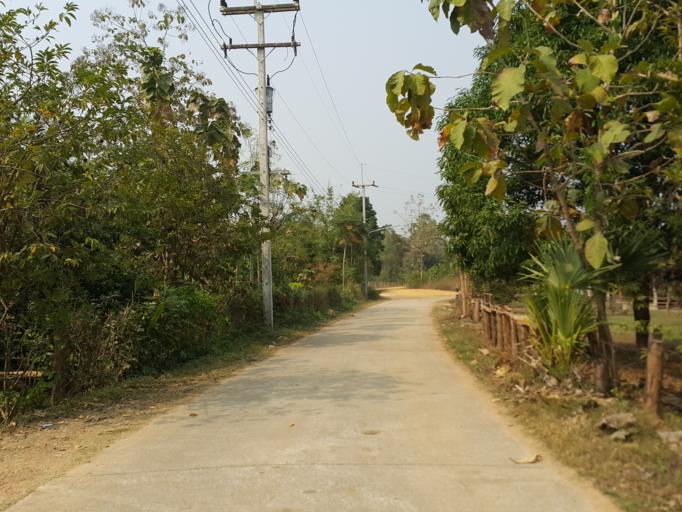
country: TH
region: Lampang
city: Mae Phrik
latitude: 17.4858
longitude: 99.0885
